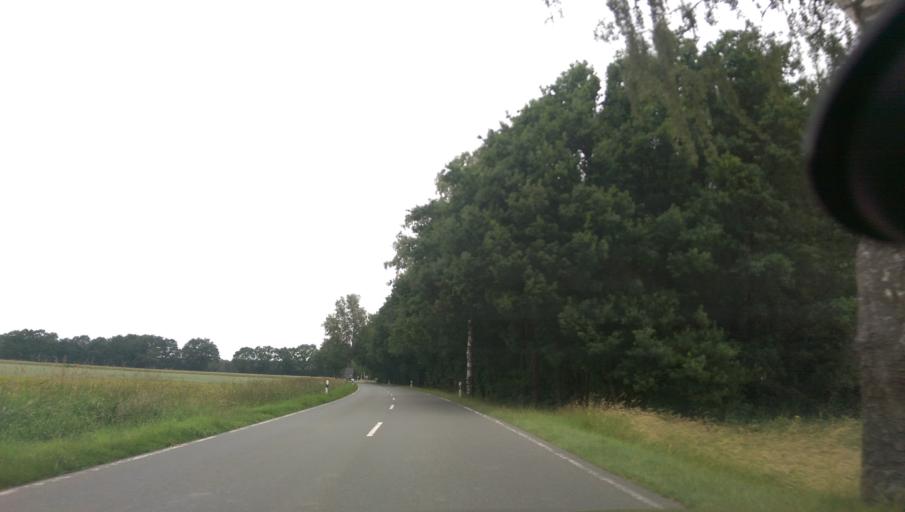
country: DE
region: Lower Saxony
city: Bomlitz
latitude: 52.9411
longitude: 9.6839
